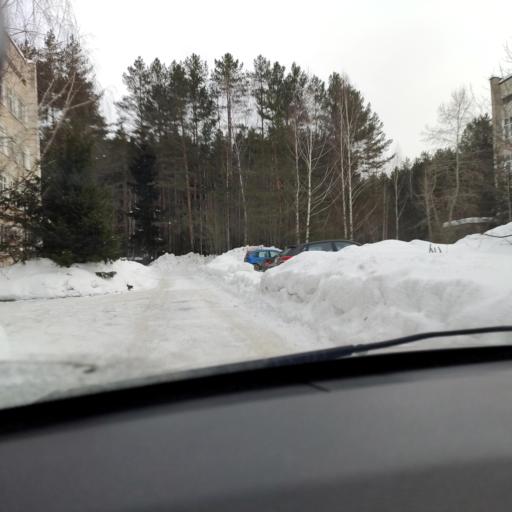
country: RU
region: Perm
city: Perm
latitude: 58.0543
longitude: 56.2252
